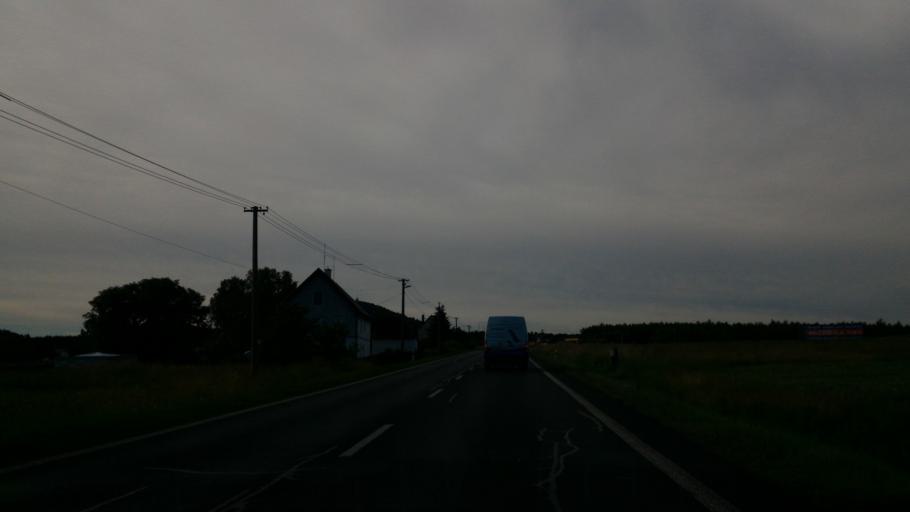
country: CZ
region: Liberecky
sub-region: Okres Ceska Lipa
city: Ceska Lipa
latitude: 50.7197
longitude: 14.5456
